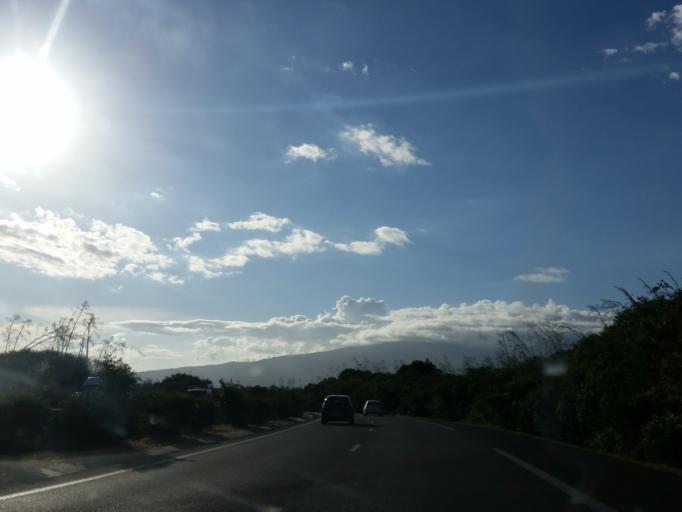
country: RE
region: Reunion
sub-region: Reunion
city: Saint-Pierre
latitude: -21.3194
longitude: 55.4461
